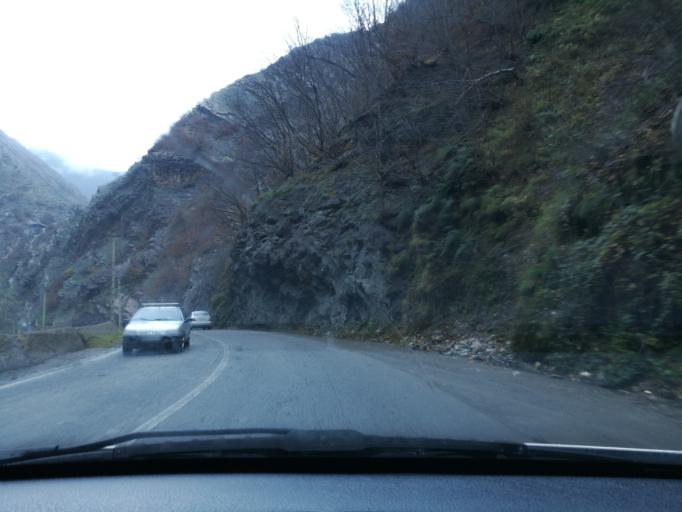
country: IR
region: Mazandaran
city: Chalus
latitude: 36.2772
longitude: 51.2444
